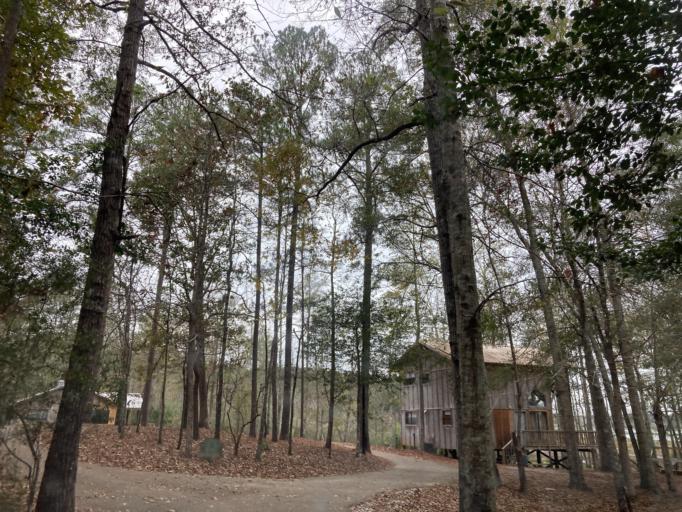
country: US
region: Mississippi
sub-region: Lamar County
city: Lumberton
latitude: 31.0826
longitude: -89.4997
